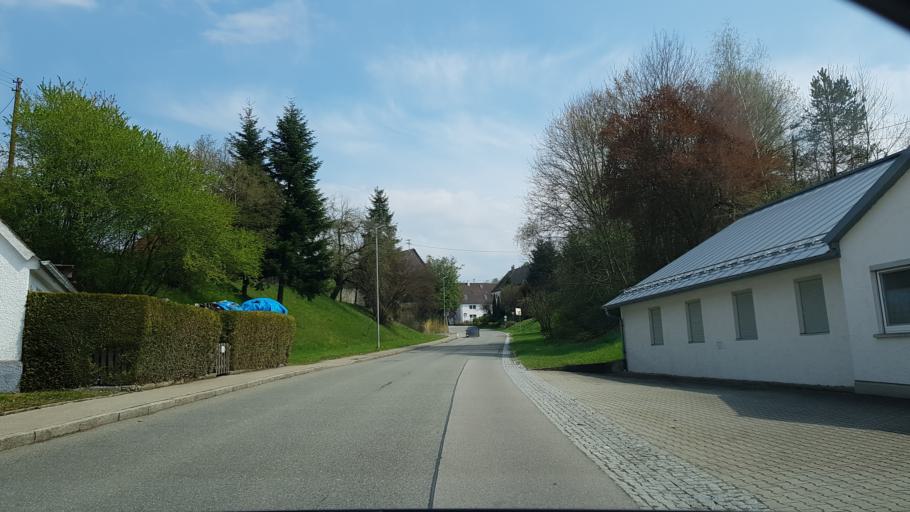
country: DE
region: Baden-Wuerttemberg
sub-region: Tuebingen Region
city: Wain
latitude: 48.2125
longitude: 10.0179
